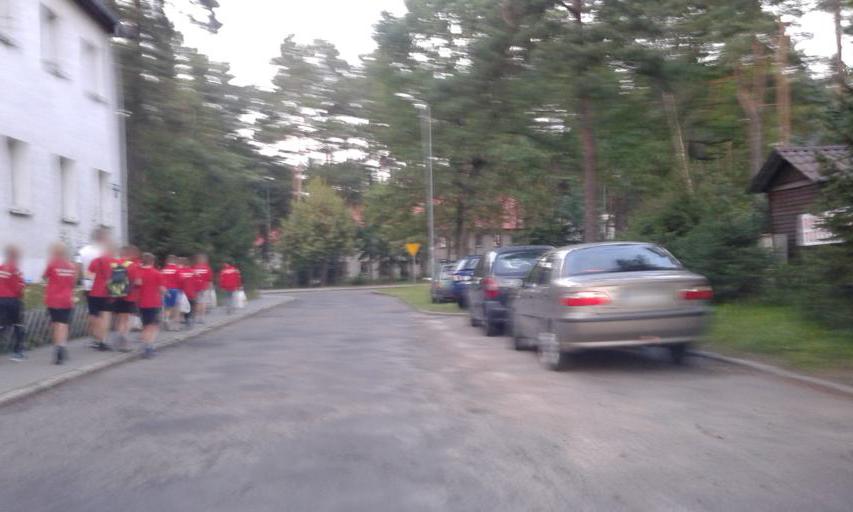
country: PL
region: West Pomeranian Voivodeship
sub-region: Powiat szczecinecki
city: Borne Sulinowo
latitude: 53.5851
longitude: 16.5423
